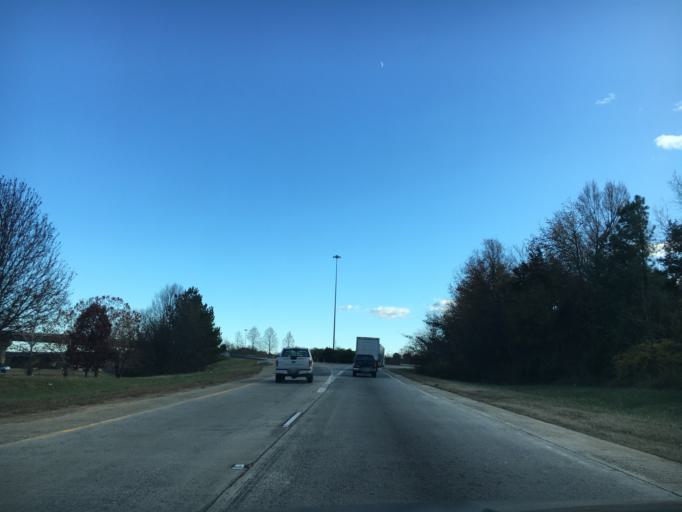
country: US
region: North Carolina
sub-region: Mecklenburg County
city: Pineville
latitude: 35.1269
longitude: -80.9207
